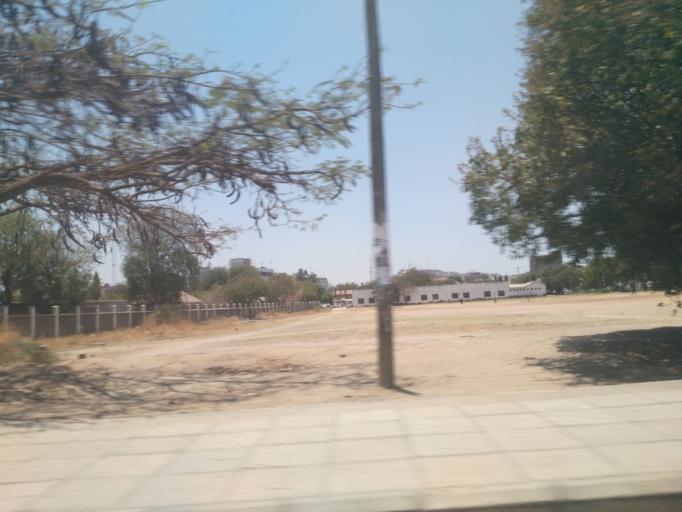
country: TZ
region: Dodoma
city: Dodoma
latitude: -6.1735
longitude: 35.7465
